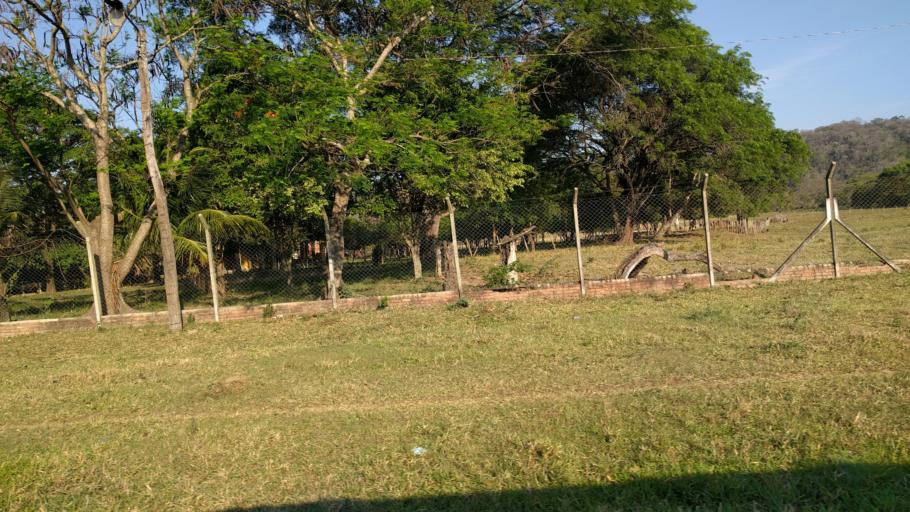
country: BO
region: Santa Cruz
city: Jorochito
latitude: -18.1041
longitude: -63.4556
